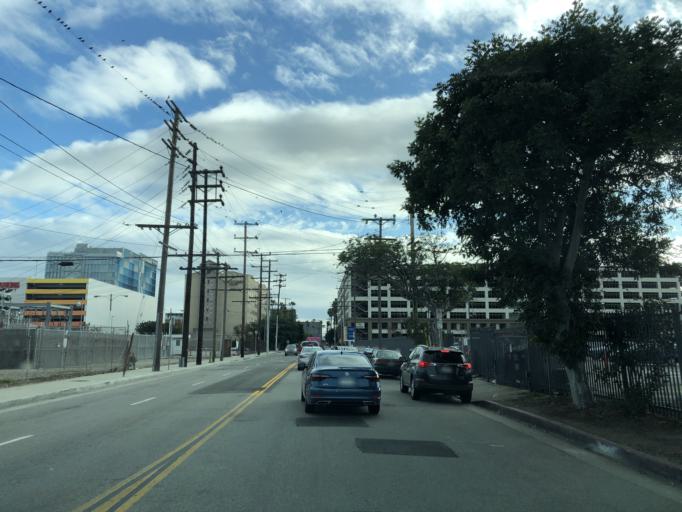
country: US
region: California
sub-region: Los Angeles County
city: El Segundo
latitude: 33.9487
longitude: -118.3940
